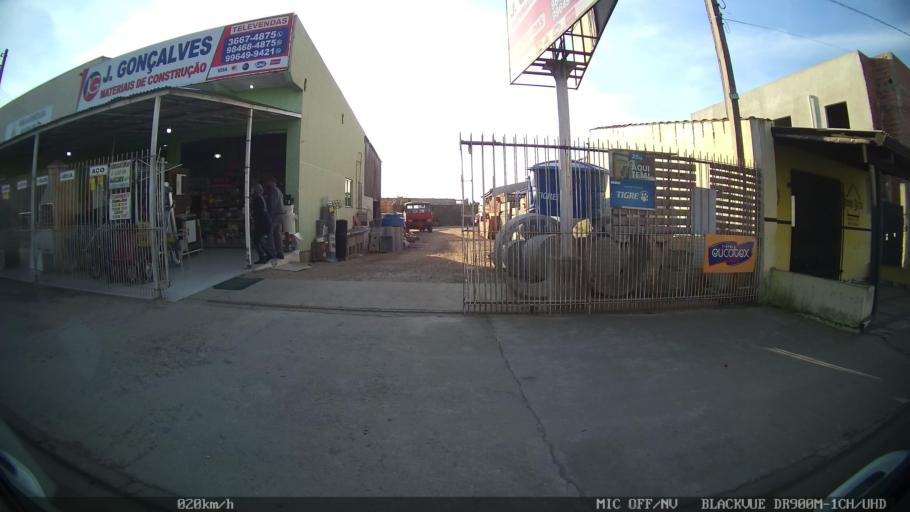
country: BR
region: Parana
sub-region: Pinhais
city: Pinhais
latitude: -25.4488
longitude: -49.1436
